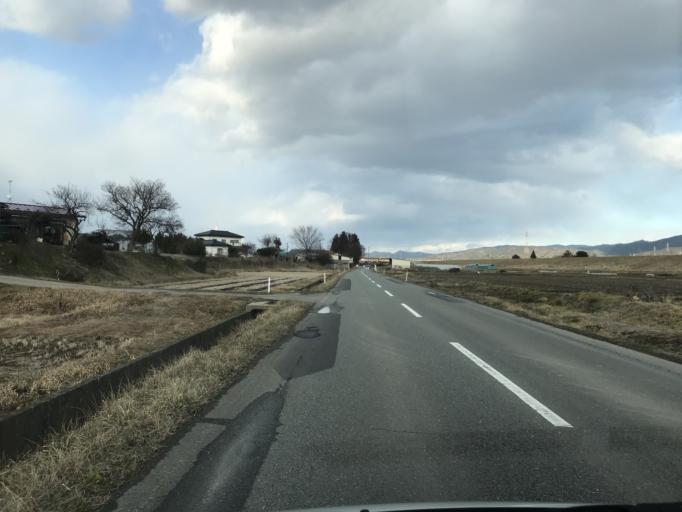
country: JP
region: Iwate
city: Mizusawa
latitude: 39.0629
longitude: 141.1577
